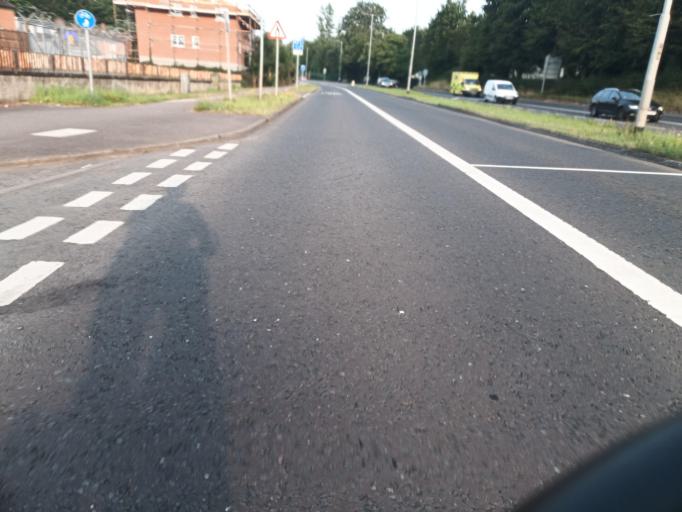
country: GB
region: Northern Ireland
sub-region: Castlereagh District
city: Dundonald
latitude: 54.5949
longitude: -5.8133
